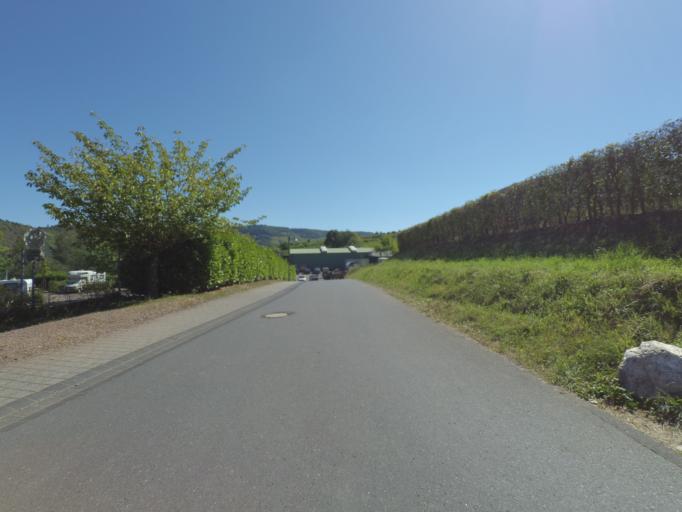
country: DE
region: Rheinland-Pfalz
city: Bremm
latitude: 50.0954
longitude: 7.1232
